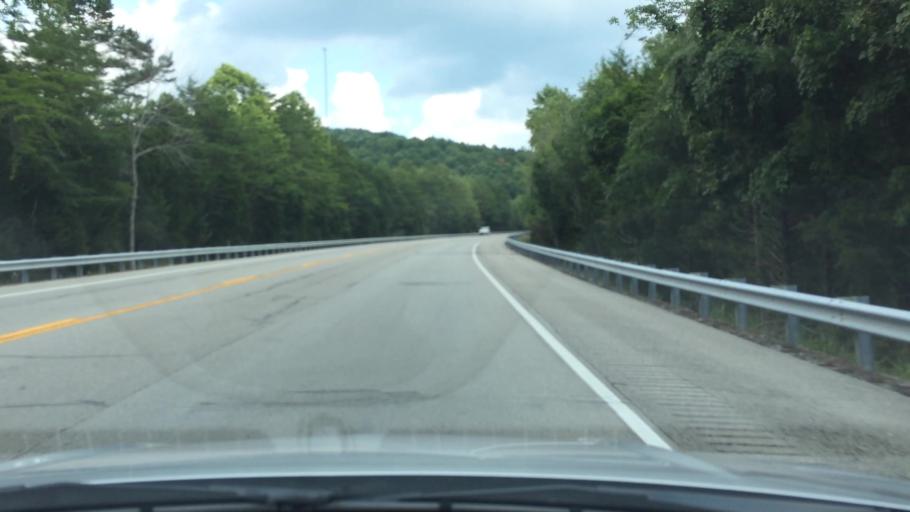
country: US
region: Kentucky
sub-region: Pulaski County
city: Somerset
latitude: 36.9378
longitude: -84.5312
